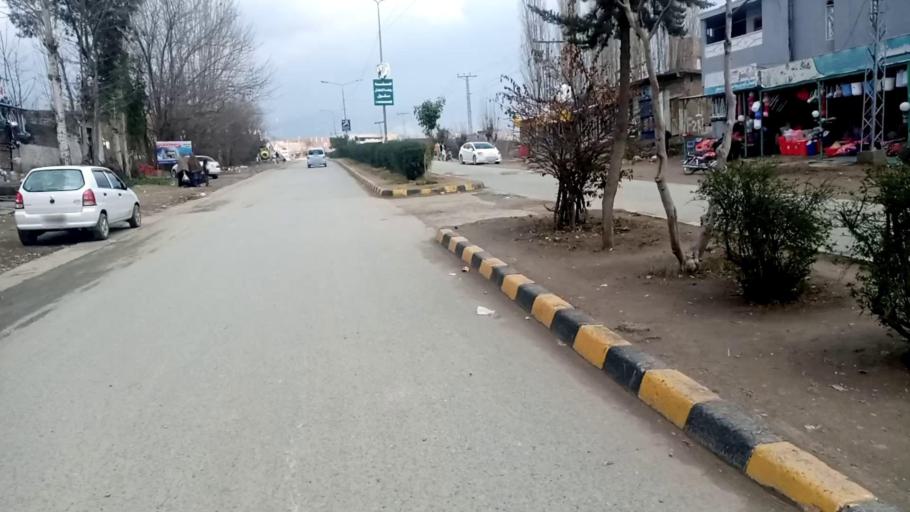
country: PK
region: Khyber Pakhtunkhwa
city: Mingora
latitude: 34.8103
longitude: 72.3409
